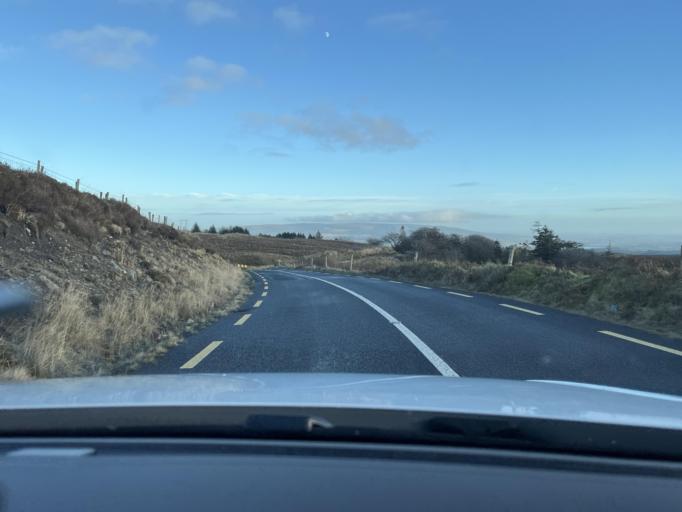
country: IE
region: Ulster
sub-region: An Cabhan
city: Ballyconnell
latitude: 54.1668
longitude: -7.8091
